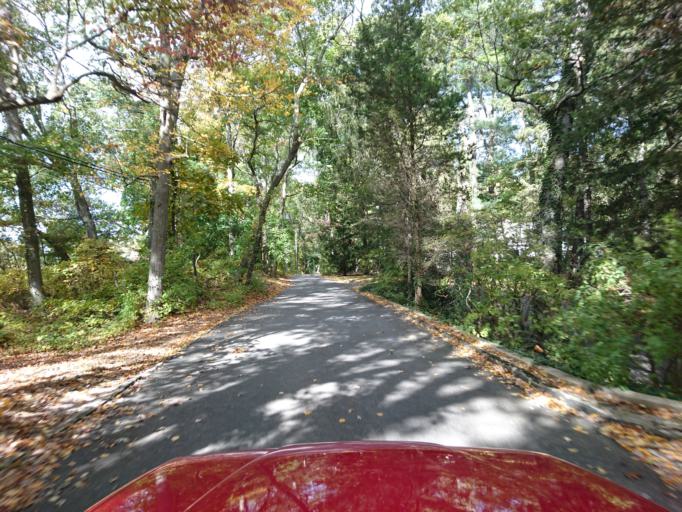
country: US
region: New York
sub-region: Nassau County
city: Upper Brookville
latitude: 40.8522
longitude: -73.5784
